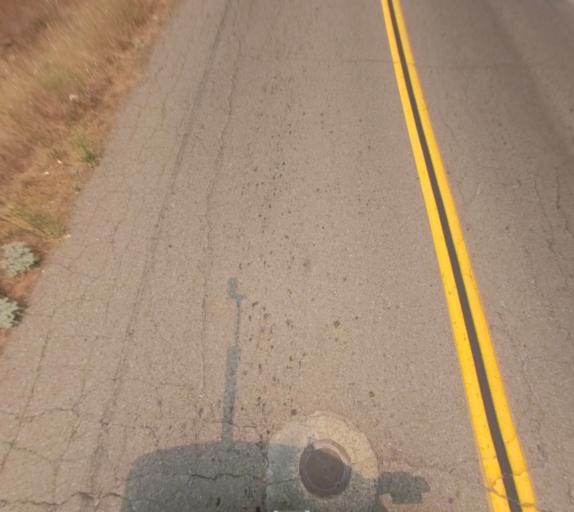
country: US
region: California
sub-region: Madera County
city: Oakhurst
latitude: 37.3291
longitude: -119.6635
